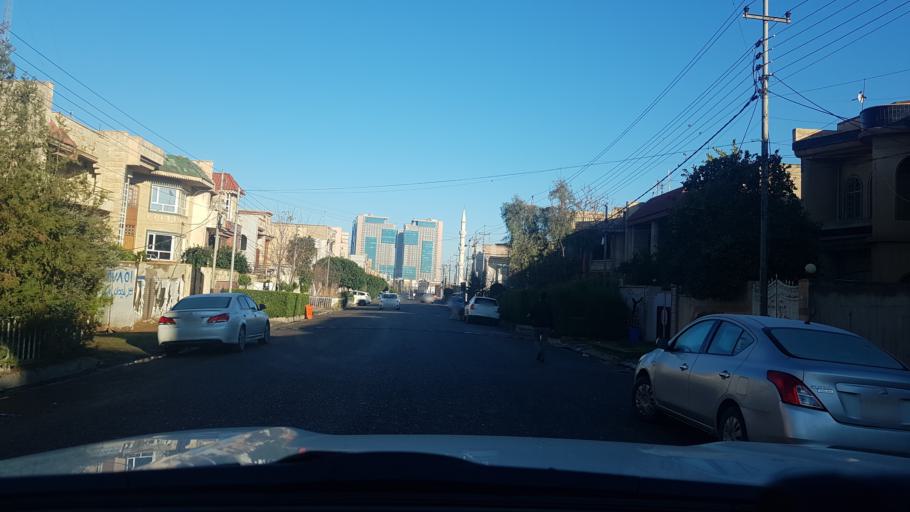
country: IQ
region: Arbil
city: Erbil
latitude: 36.2072
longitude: 44.0071
